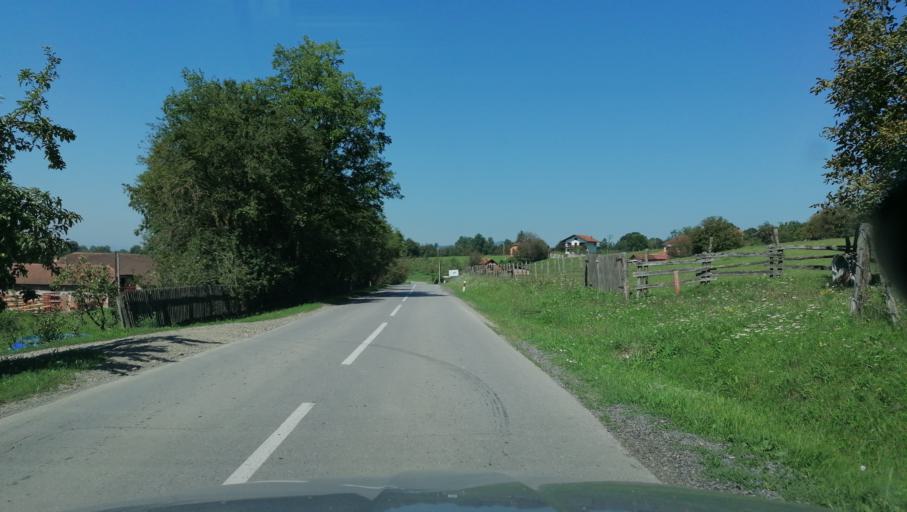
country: RS
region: Central Serbia
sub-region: Raski Okrug
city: Vrnjacka Banja
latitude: 43.7054
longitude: 20.8464
